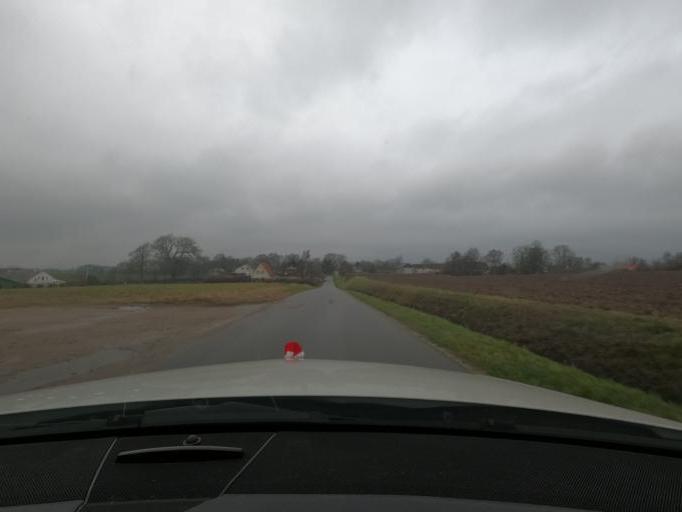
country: DK
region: South Denmark
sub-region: Haderslev Kommune
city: Starup
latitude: 55.1998
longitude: 9.6392
